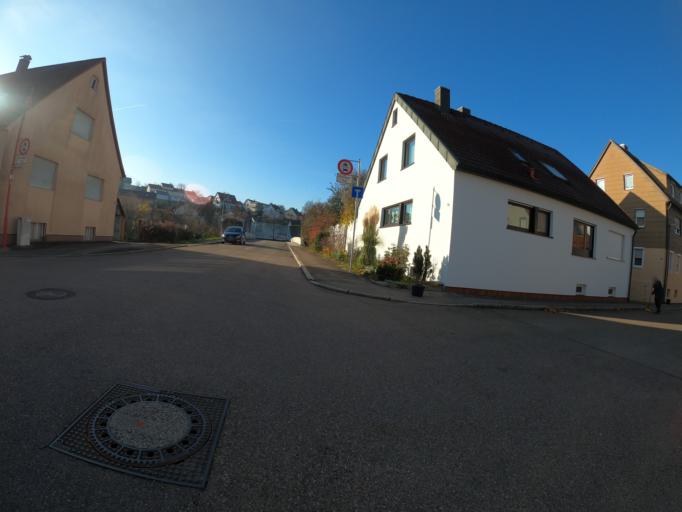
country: DE
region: Baden-Wuerttemberg
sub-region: Regierungsbezirk Stuttgart
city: Uhingen
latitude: 48.7056
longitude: 9.5797
